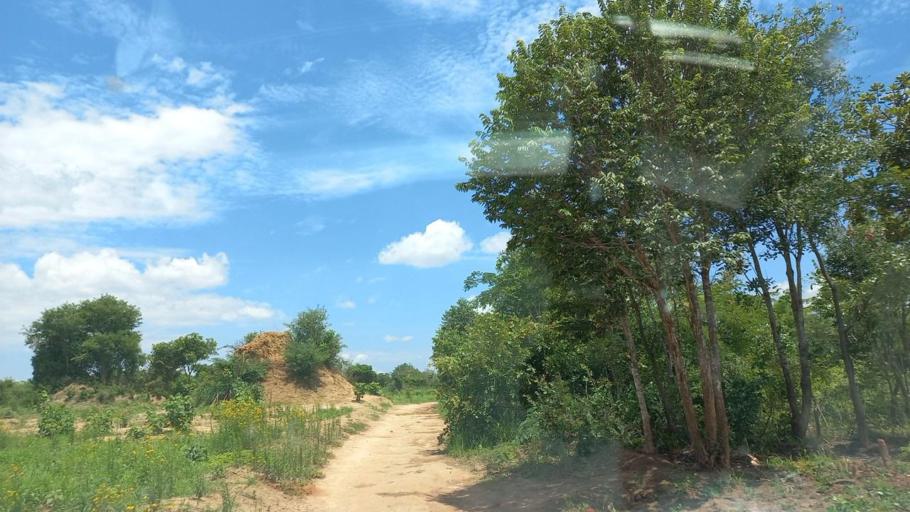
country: ZM
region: Copperbelt
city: Ndola
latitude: -12.8796
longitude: 28.4492
